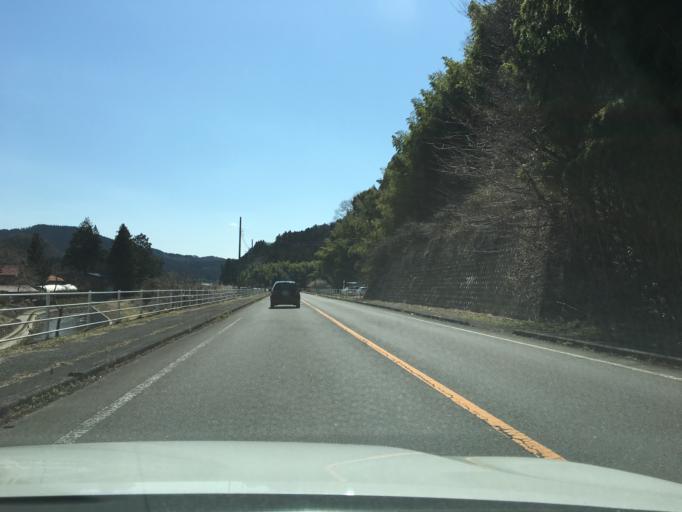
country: JP
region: Tochigi
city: Kuroiso
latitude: 37.0179
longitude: 140.1779
